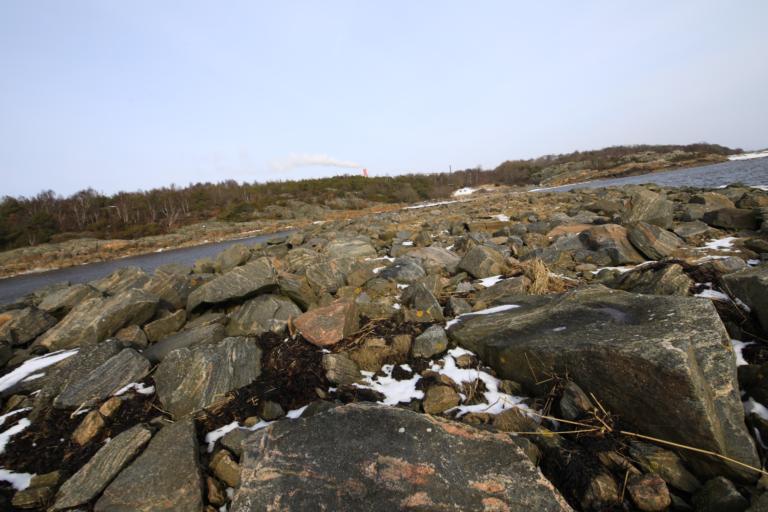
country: SE
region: Halland
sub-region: Kungsbacka Kommun
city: Frillesas
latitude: 57.2144
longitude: 12.1665
